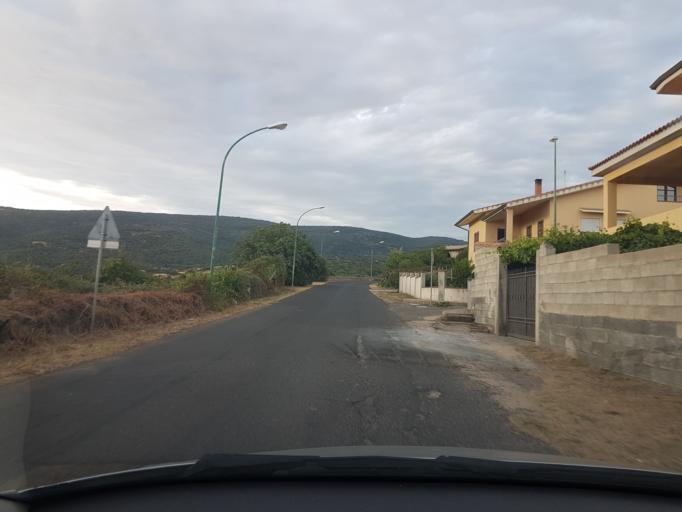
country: IT
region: Sardinia
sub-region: Provincia di Oristano
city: Seneghe
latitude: 40.0809
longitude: 8.6068
